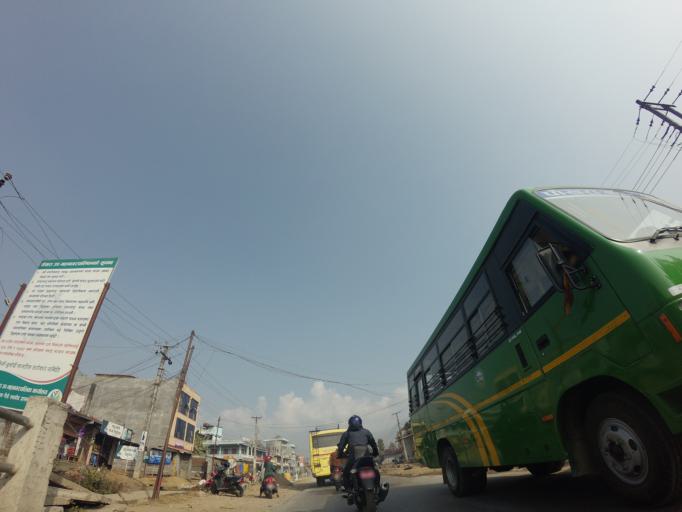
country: NP
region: Western Region
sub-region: Gandaki Zone
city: Pokhara
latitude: 28.2286
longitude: 83.9814
